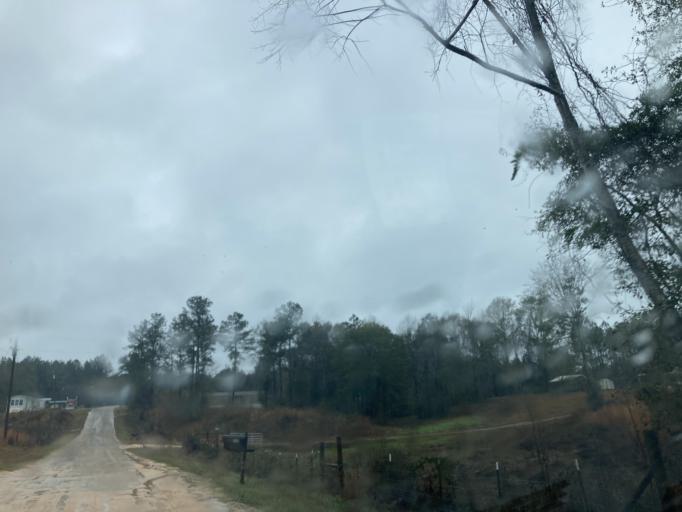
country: US
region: Mississippi
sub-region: Forrest County
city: Rawls Springs
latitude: 31.4384
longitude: -89.3483
